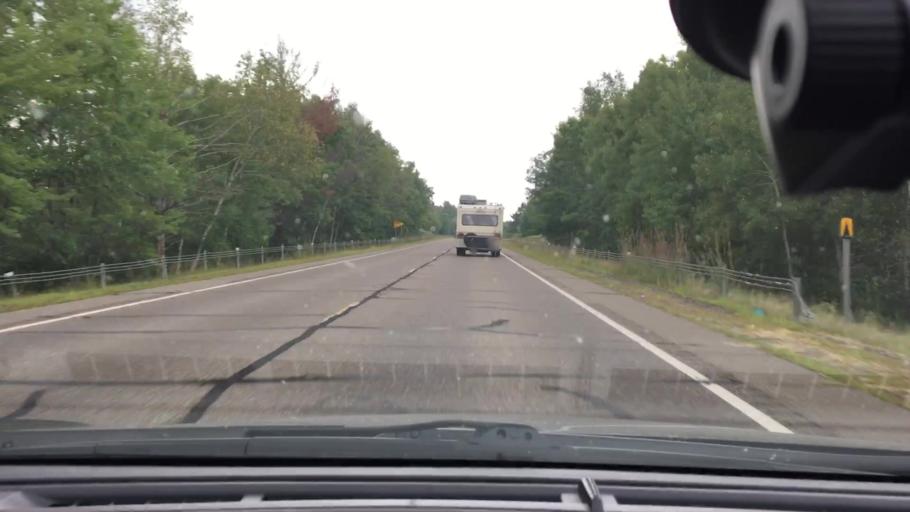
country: US
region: Minnesota
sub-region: Crow Wing County
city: Crosby
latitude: 46.4391
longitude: -93.8758
